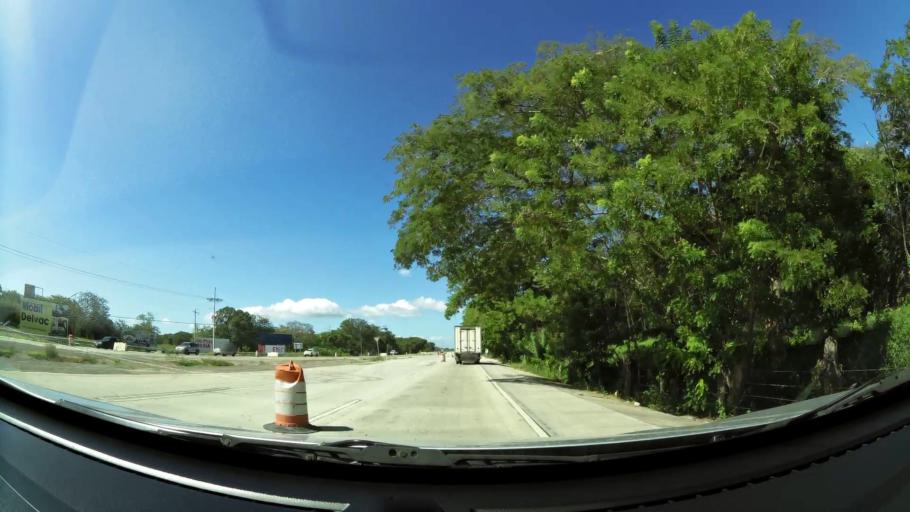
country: CR
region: Guanacaste
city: Liberia
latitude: 10.6015
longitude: -85.4272
